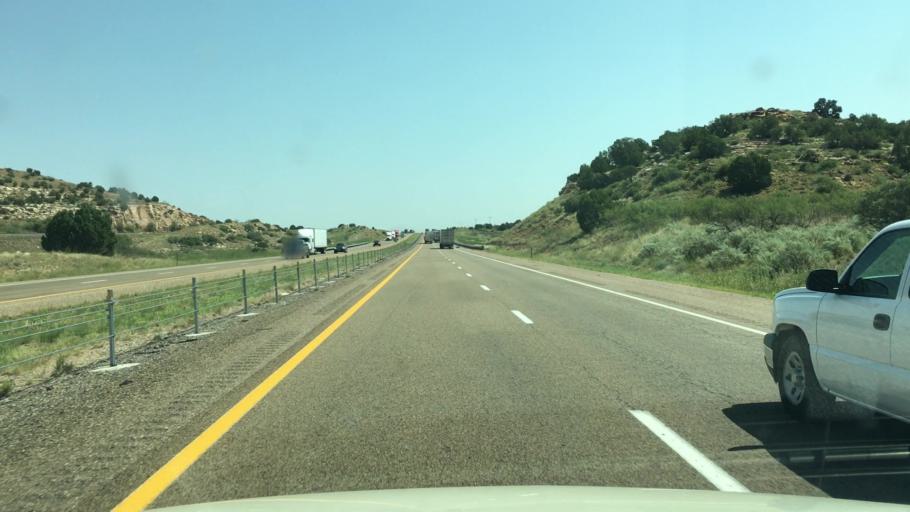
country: US
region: New Mexico
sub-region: Quay County
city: Tucumcari
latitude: 35.1196
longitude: -103.8630
